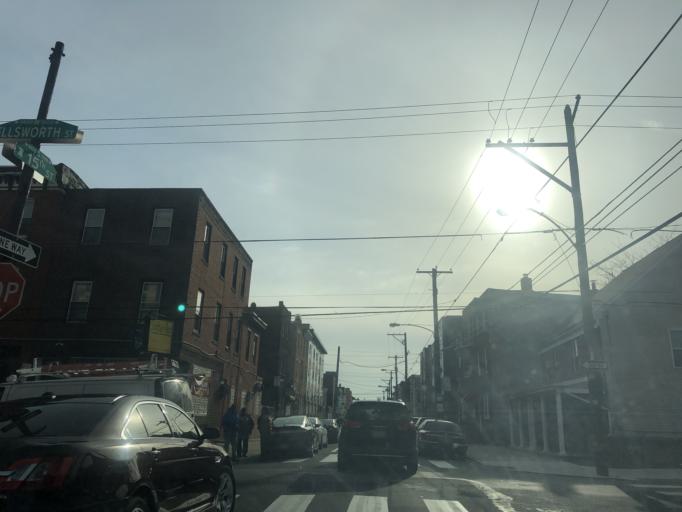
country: US
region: Pennsylvania
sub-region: Philadelphia County
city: Philadelphia
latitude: 39.9372
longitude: -75.1687
